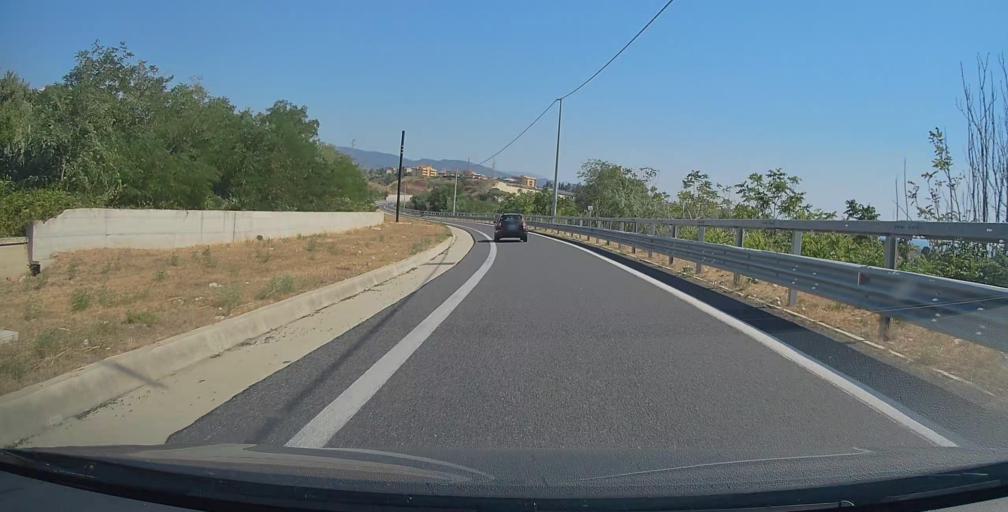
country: IT
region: Calabria
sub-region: Provincia di Reggio Calabria
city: Campo Calabro
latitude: 38.2249
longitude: 15.6450
